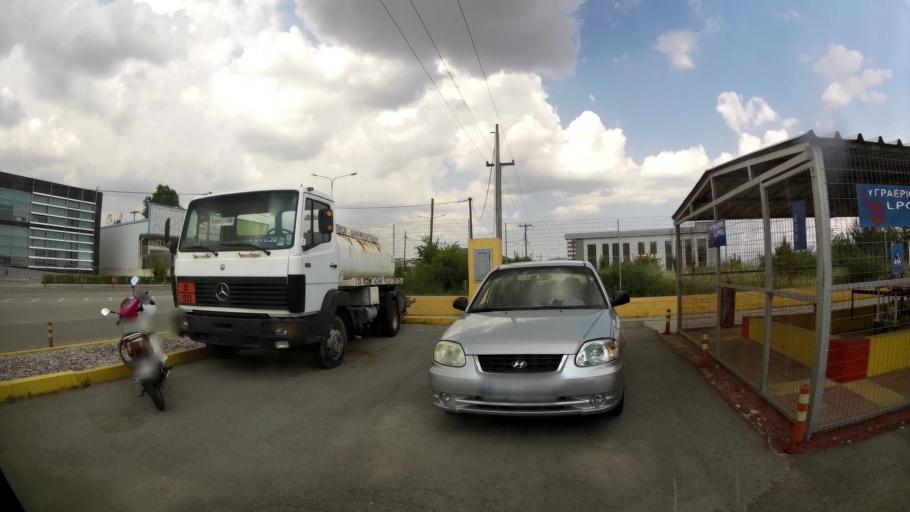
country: GR
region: West Macedonia
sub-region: Nomos Kozanis
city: Kozani
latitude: 40.3072
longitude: 21.8111
